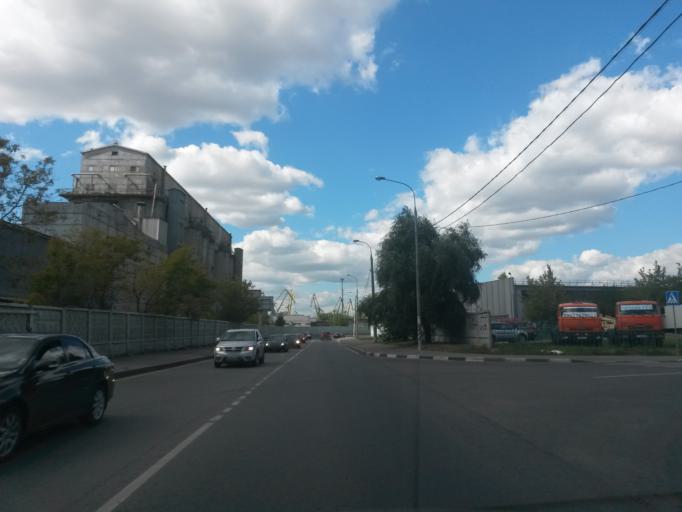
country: RU
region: Moscow
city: Tekstil'shchiki
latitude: 55.6914
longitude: 37.7172
